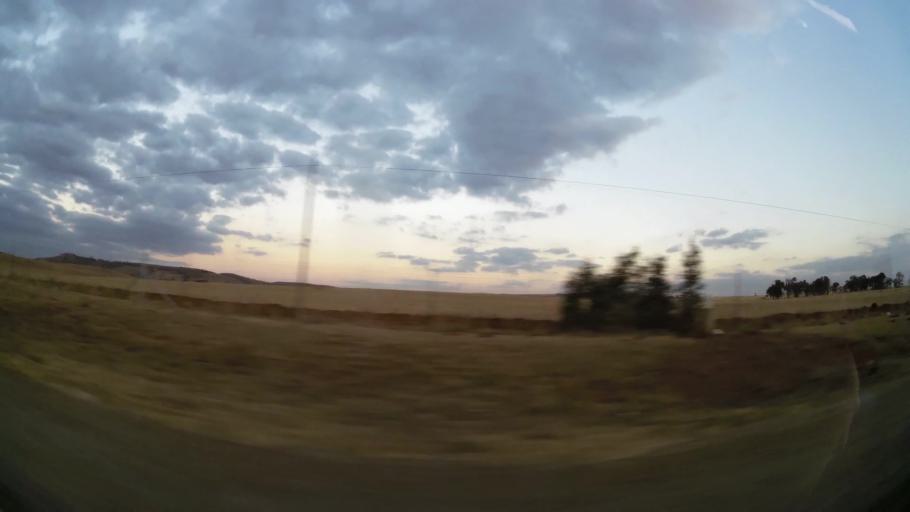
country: ZA
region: Gauteng
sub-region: West Rand District Municipality
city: Krugersdorp
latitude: -26.0562
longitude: 27.7059
